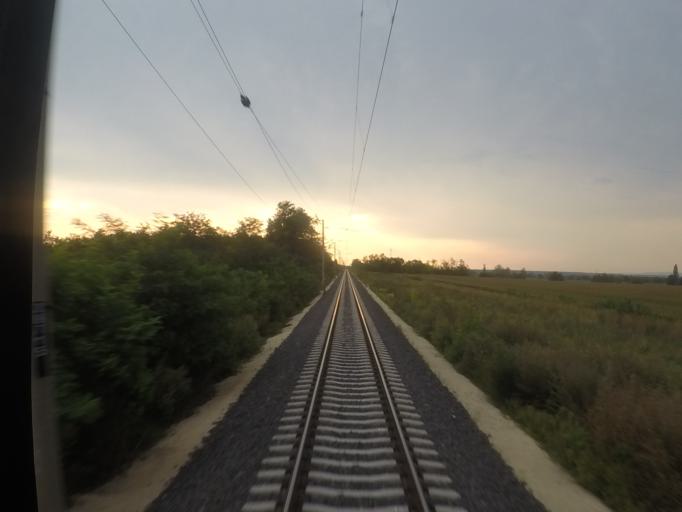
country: HU
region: Fejer
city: Lepseny
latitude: 46.9750
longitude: 18.2158
